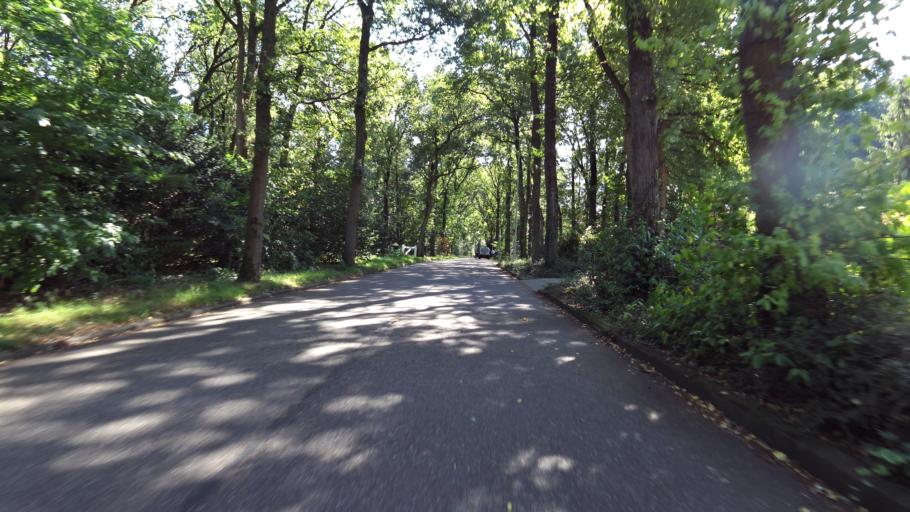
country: NL
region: Gelderland
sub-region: Gemeente Renkum
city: Heelsum
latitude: 51.9861
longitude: 5.7601
